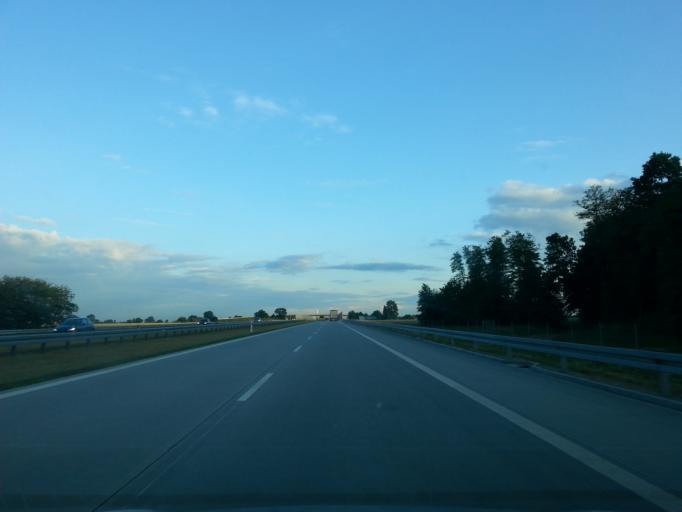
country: PL
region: Lodz Voivodeship
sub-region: Powiat sieradzki
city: Zloczew
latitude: 51.4346
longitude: 18.6457
